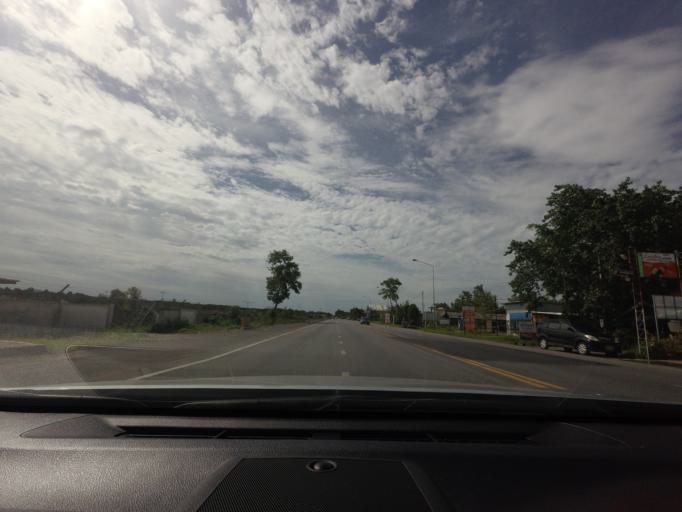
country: TH
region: Songkhla
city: Khlong Hoi Khong
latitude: 6.9328
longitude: 100.4158
